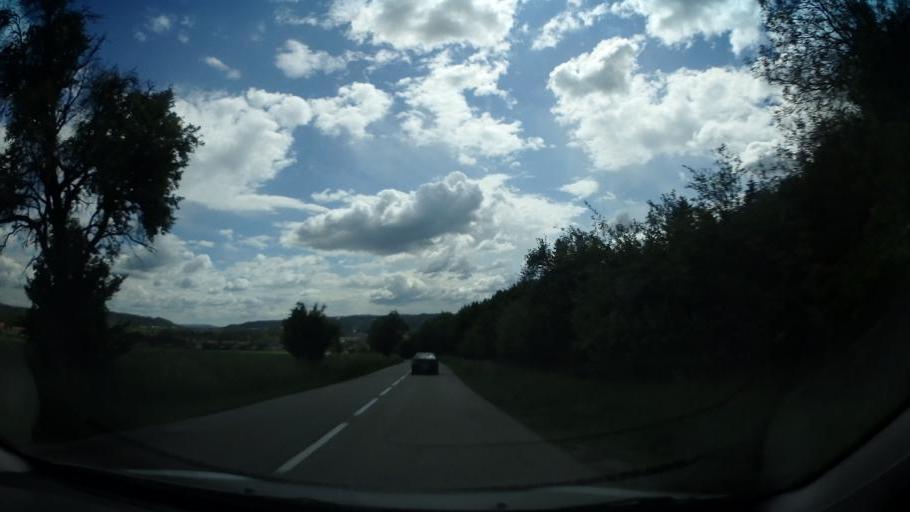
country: CZ
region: South Moravian
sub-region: Okres Blansko
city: Letovice
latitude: 49.5657
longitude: 16.5809
